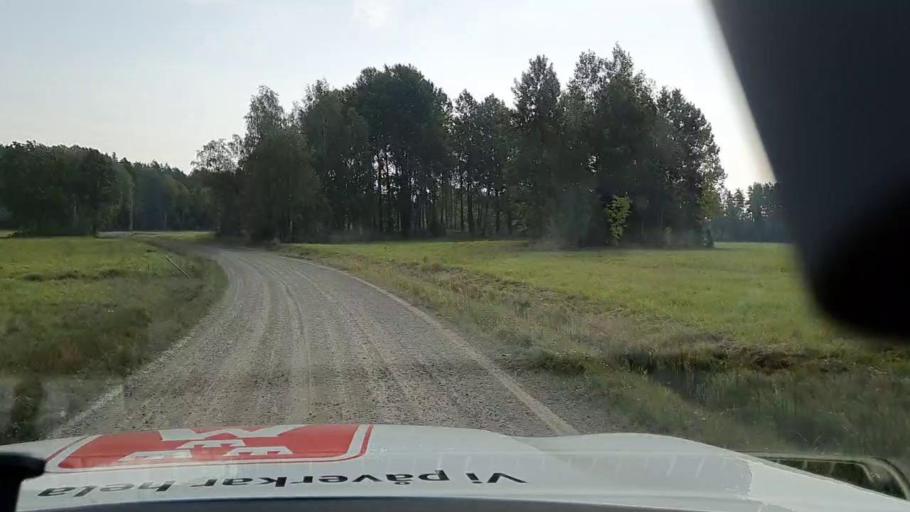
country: SE
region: Vaestmanland
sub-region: Kungsors Kommun
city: Kungsoer
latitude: 59.3604
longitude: 16.1440
